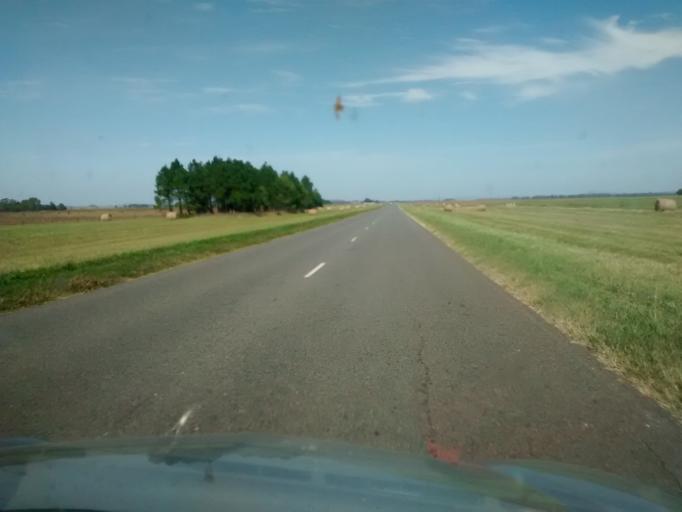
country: AR
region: Buenos Aires
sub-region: Partido de Balcarce
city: Balcarce
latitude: -37.6048
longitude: -58.5012
